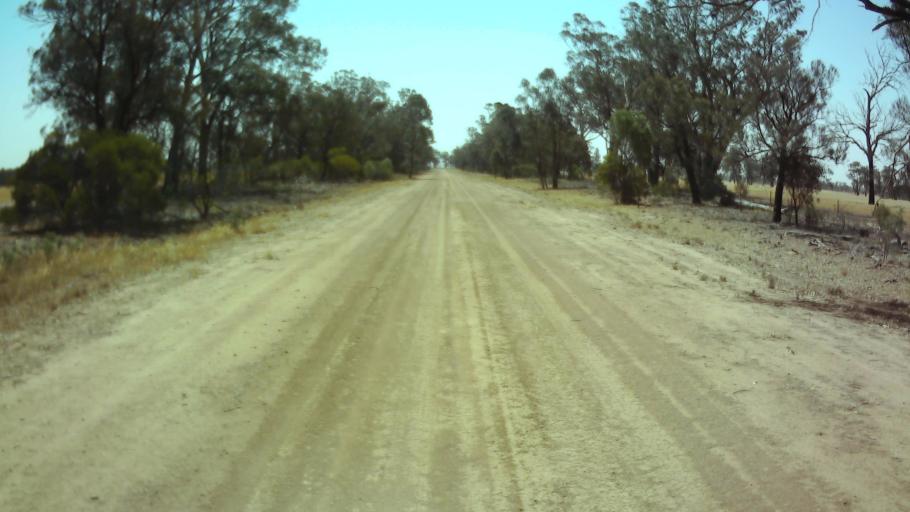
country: AU
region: New South Wales
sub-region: Weddin
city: Grenfell
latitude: -33.9413
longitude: 147.8118
